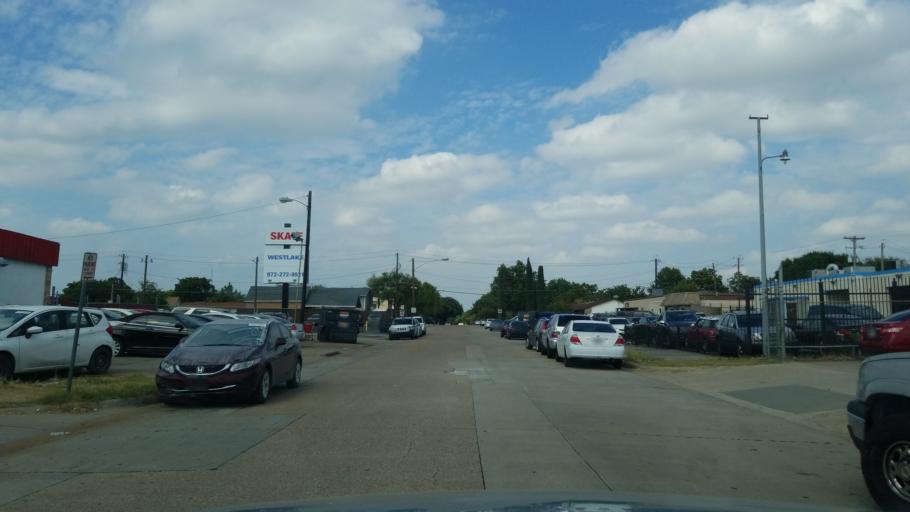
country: US
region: Texas
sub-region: Dallas County
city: Garland
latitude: 32.9094
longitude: -96.6923
